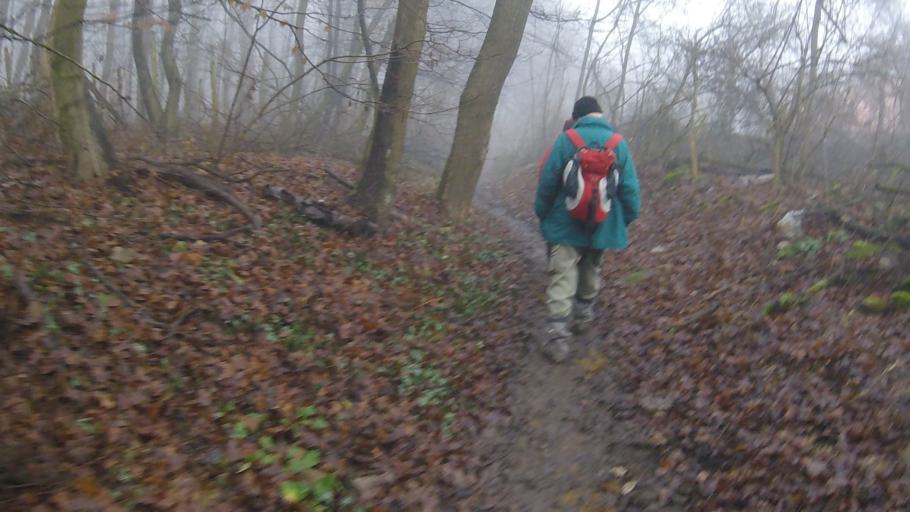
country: HU
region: Pest
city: Budakeszi
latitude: 47.5361
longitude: 18.9343
